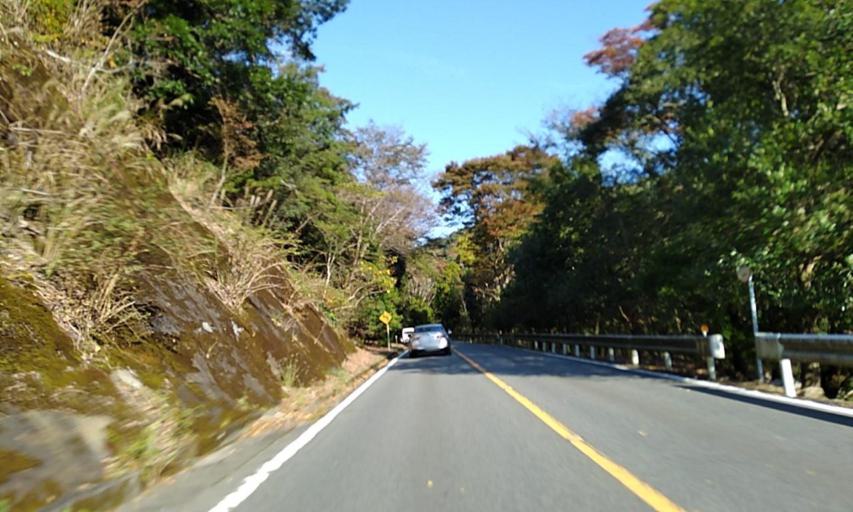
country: JP
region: Mie
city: Ise
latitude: 34.4492
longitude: 136.7491
